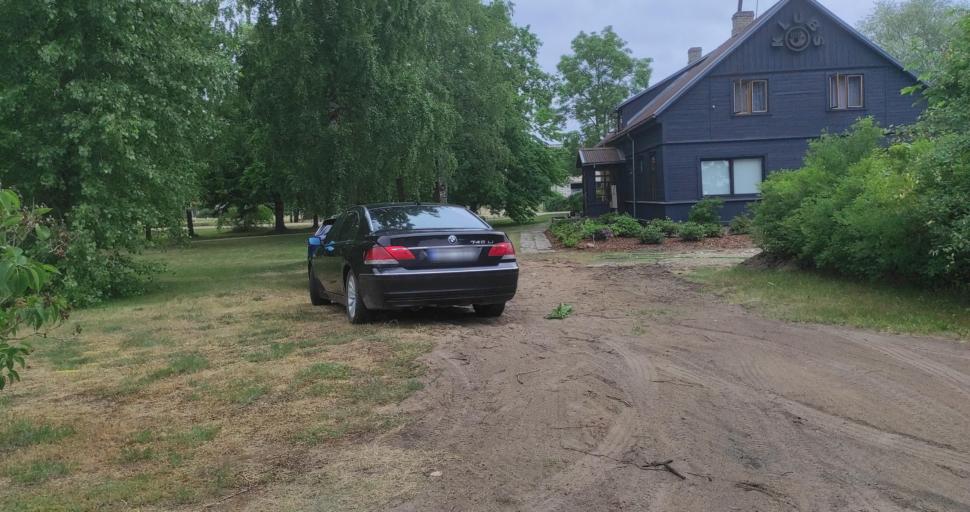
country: LV
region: Pavilostas
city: Pavilosta
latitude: 56.8894
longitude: 21.1804
